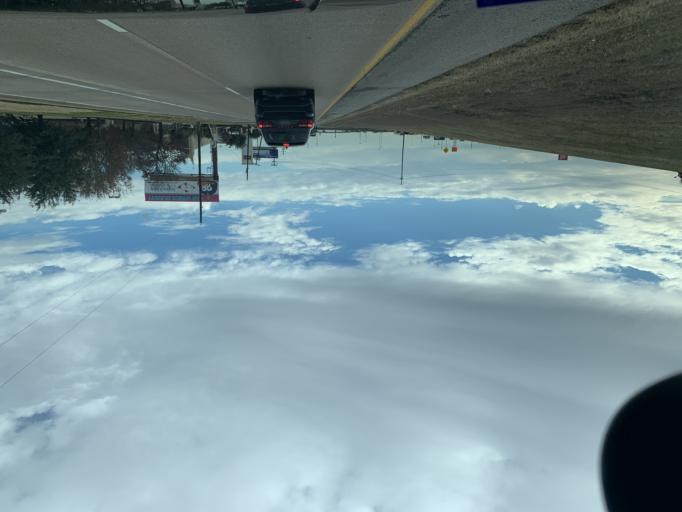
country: US
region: Texas
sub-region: Dallas County
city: Duncanville
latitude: 32.6487
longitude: -96.8636
